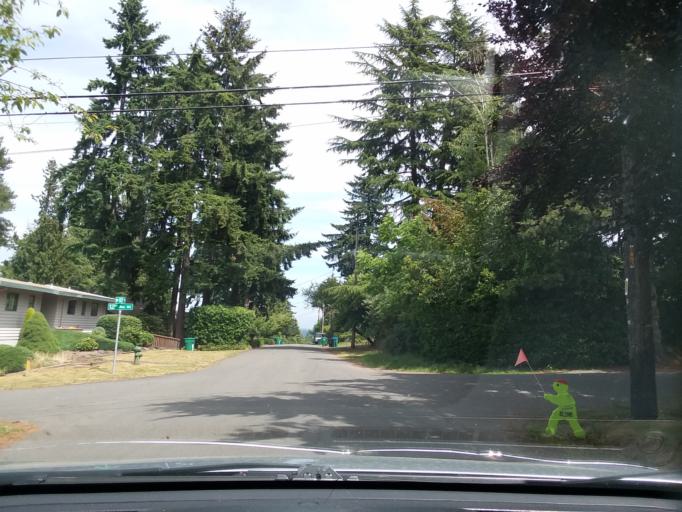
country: US
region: Washington
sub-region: King County
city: Shoreline
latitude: 47.7031
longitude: -122.3152
